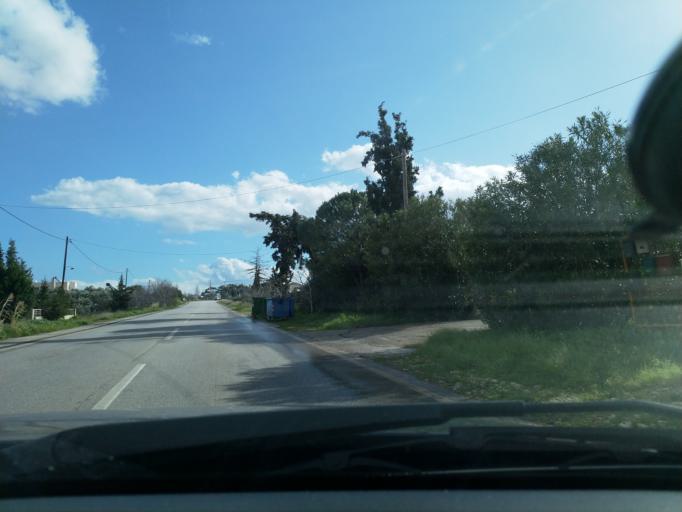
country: GR
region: Crete
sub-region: Nomos Chanias
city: Mouzouras
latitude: 35.5178
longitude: 24.1294
